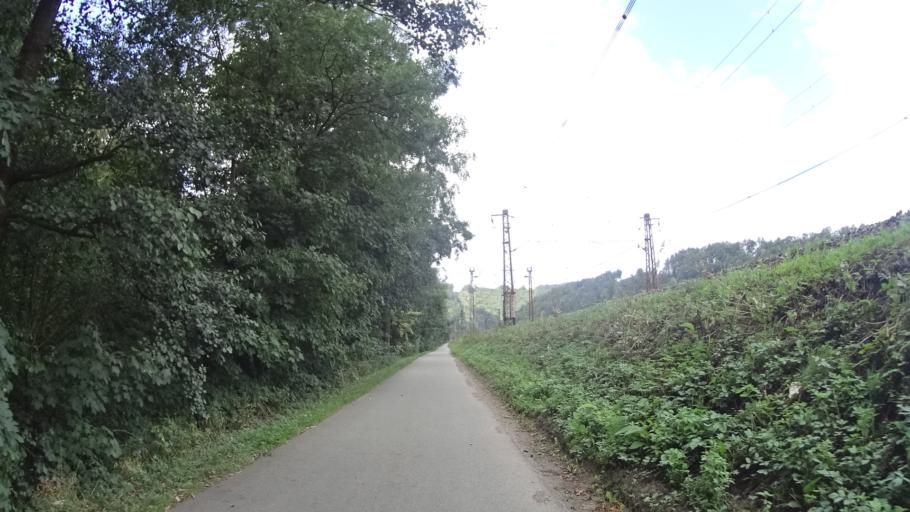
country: CZ
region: Pardubicky
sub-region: Okres Usti nad Orlici
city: Usti nad Orlici
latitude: 49.9732
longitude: 16.3542
